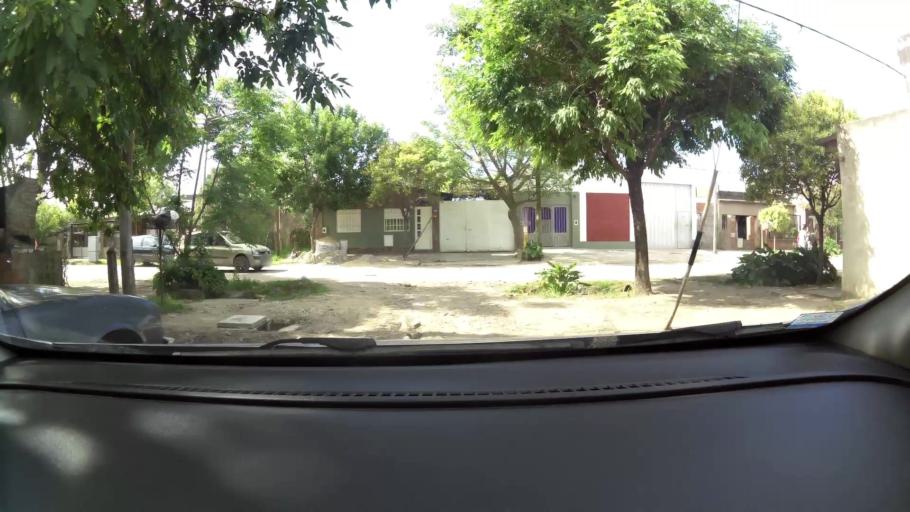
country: AR
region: Santa Fe
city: Granadero Baigorria
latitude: -32.9172
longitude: -60.7130
